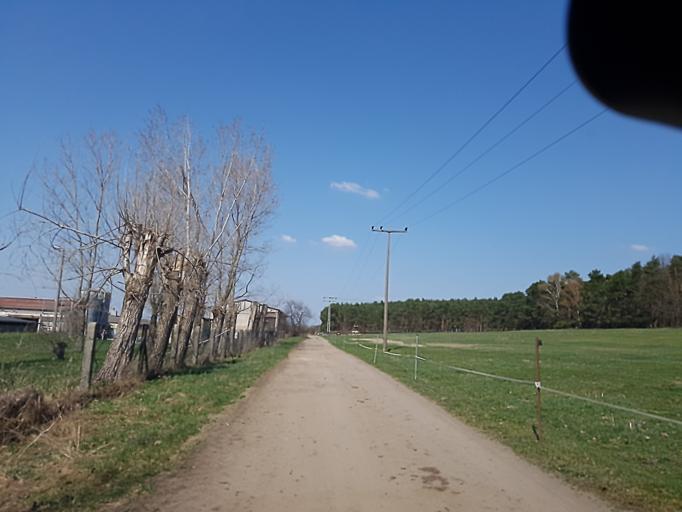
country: DE
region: Brandenburg
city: Trobitz
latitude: 51.5617
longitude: 13.4133
